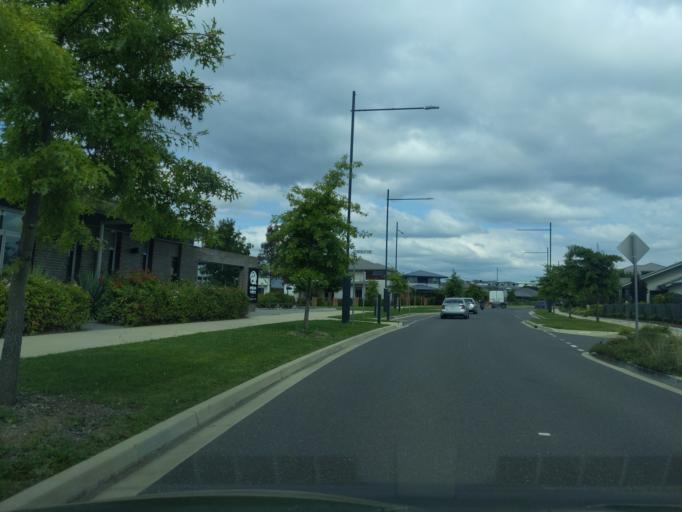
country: AU
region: New South Wales
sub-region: Queanbeyan
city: Queanbeyan
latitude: -35.4177
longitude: 149.2329
